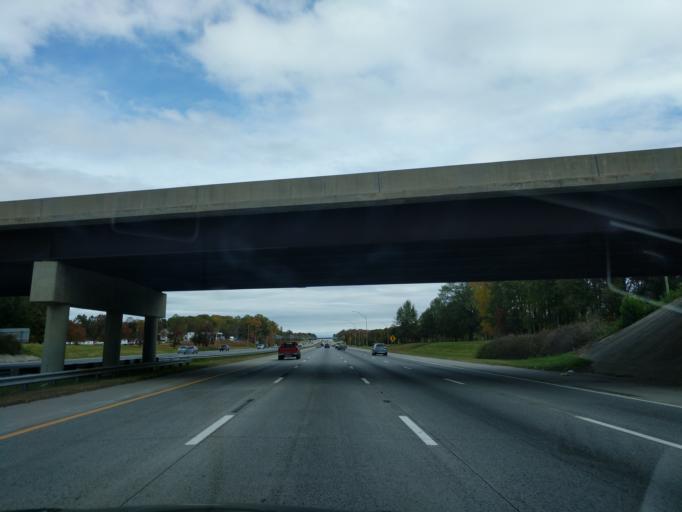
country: US
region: North Carolina
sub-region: Rowan County
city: Granite Quarry
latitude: 35.6106
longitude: -80.5183
